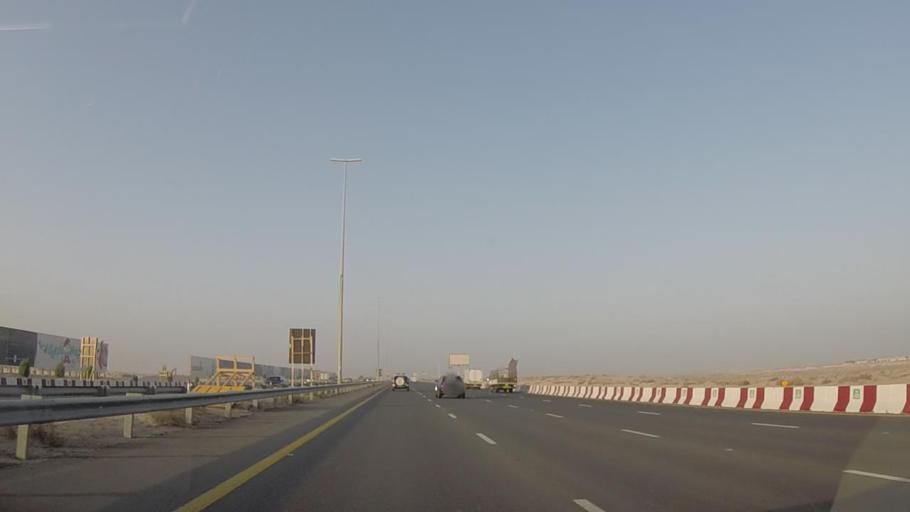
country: AE
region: Dubai
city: Dubai
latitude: 24.9201
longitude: 54.9844
